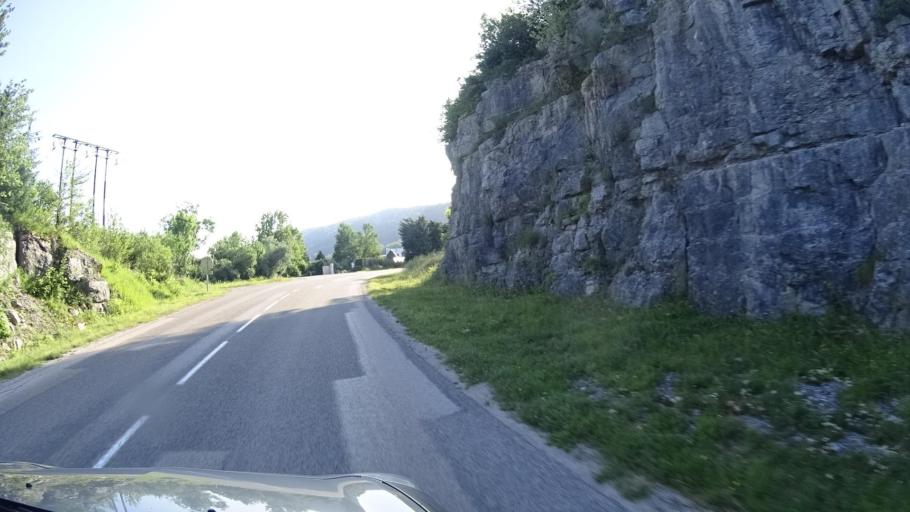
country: FR
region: Franche-Comte
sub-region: Departement du Jura
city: Morbier
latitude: 46.5363
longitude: 6.0089
